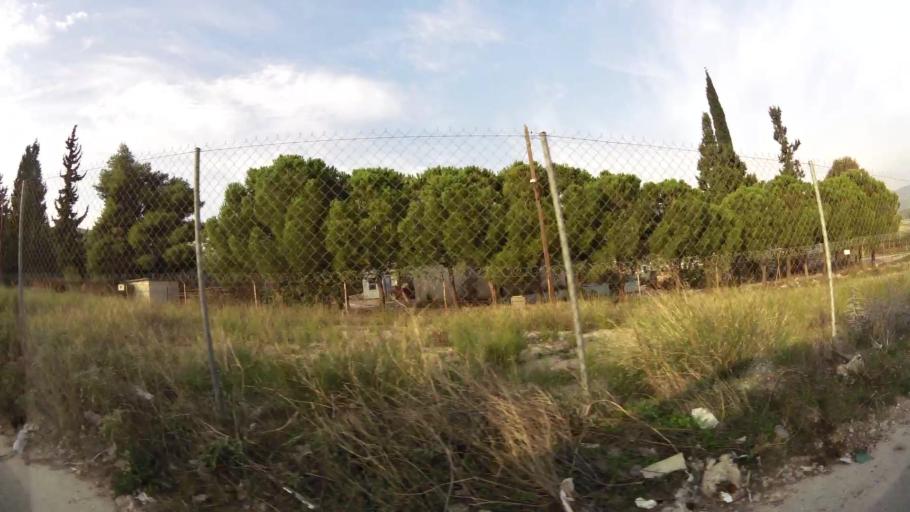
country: GR
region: Attica
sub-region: Nomarchia Dytikis Attikis
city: Ano Liosia
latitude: 38.0683
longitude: 23.6790
